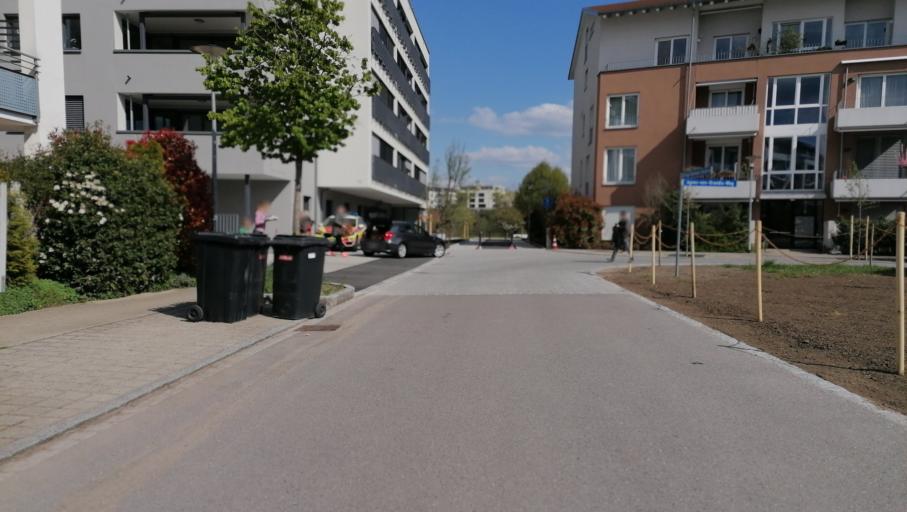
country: DE
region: Baden-Wuerttemberg
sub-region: Freiburg Region
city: Bad Sackingen
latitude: 47.5483
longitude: 7.9475
